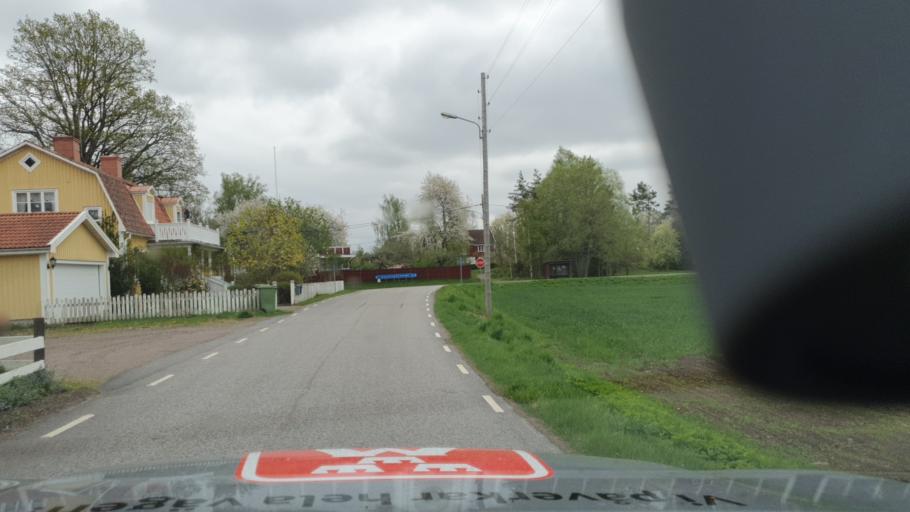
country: SE
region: Kalmar
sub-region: Vasterviks Kommun
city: Ankarsrum
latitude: 57.7766
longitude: 16.1541
